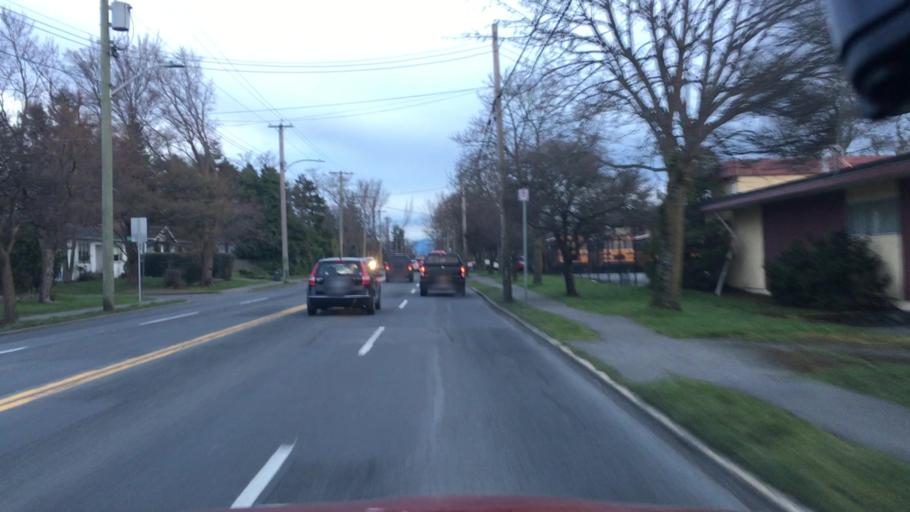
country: CA
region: British Columbia
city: Oak Bay
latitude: 48.4547
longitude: -123.3332
